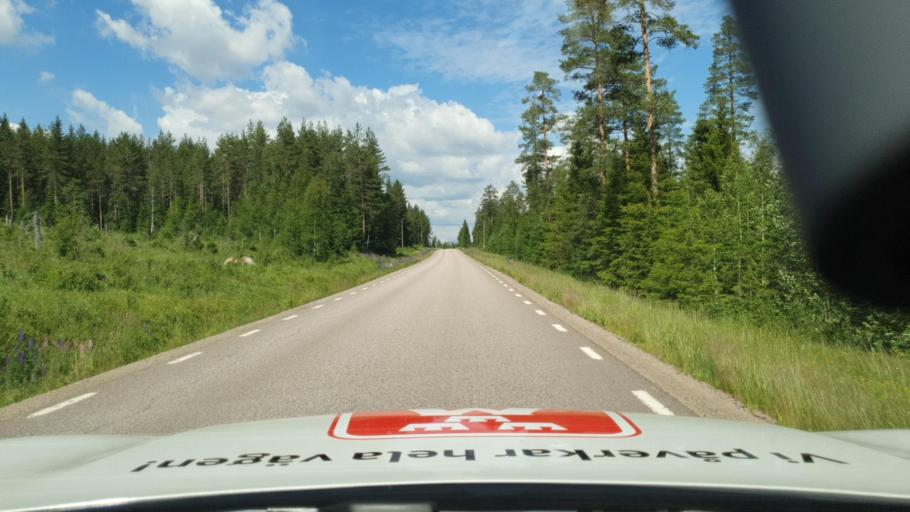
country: SE
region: Vaermland
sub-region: Torsby Kommun
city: Torsby
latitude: 60.4177
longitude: 12.9062
